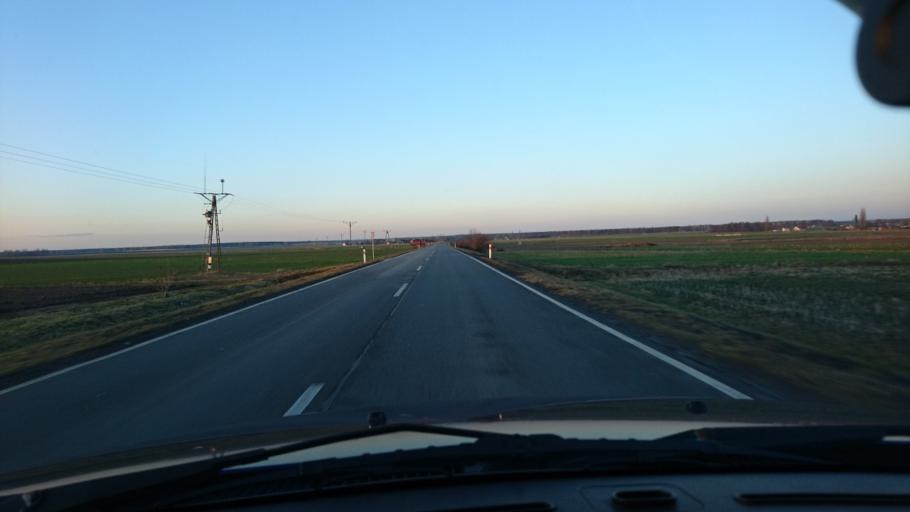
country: PL
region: Silesian Voivodeship
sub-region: Powiat gliwicki
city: Wielowies
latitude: 50.5098
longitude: 18.6047
